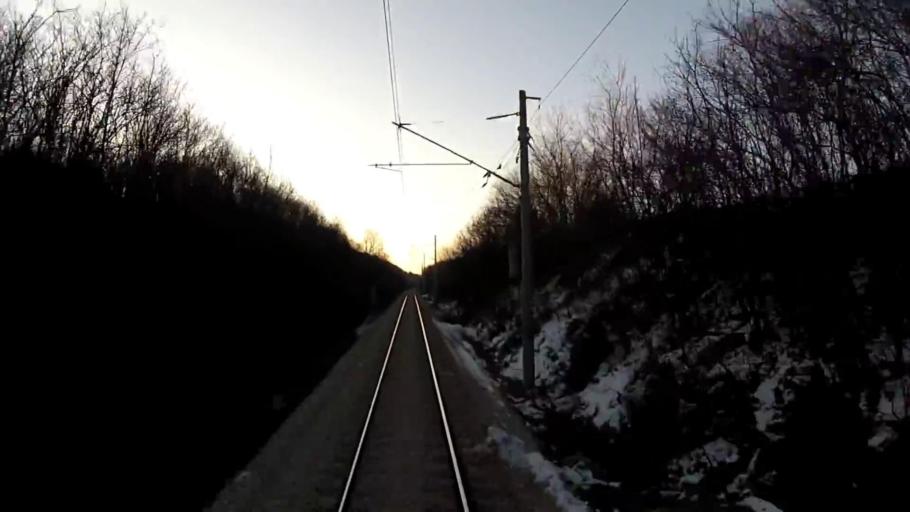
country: BG
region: Sofiya
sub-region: Obshtina Dragoman
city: Dragoman
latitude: 42.9062
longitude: 22.9458
